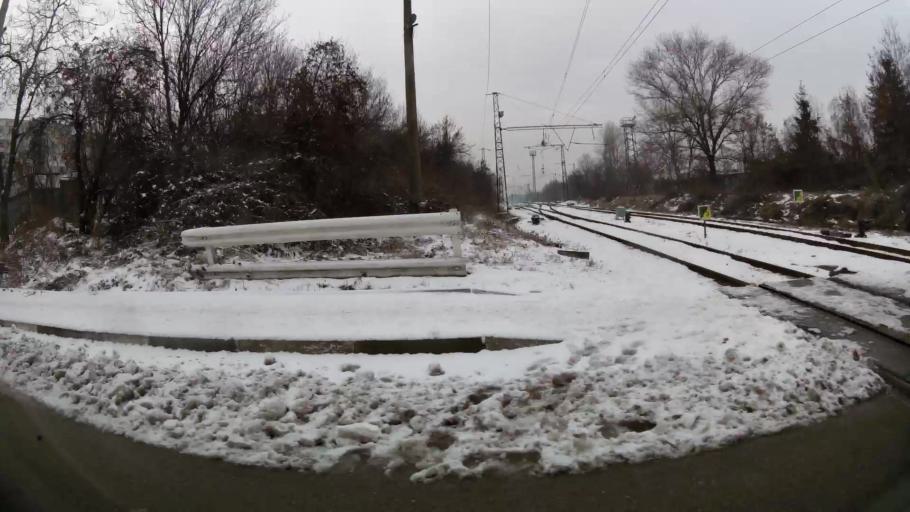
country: BG
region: Sofia-Capital
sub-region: Stolichna Obshtina
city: Sofia
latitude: 42.7149
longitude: 23.2976
